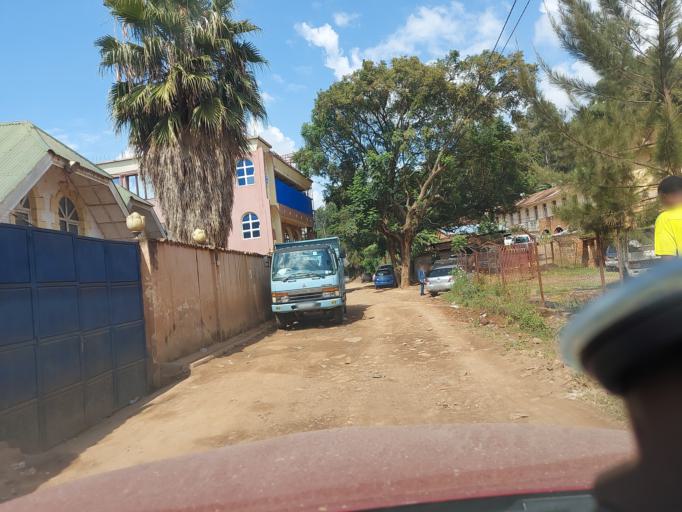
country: CD
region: South Kivu
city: Bukavu
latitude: -2.4951
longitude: 28.8626
